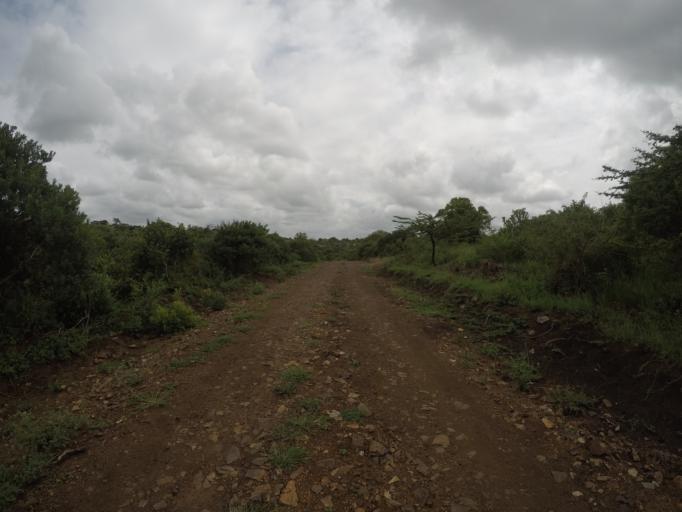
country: ZA
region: KwaZulu-Natal
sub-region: uThungulu District Municipality
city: Empangeni
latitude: -28.5852
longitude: 31.8687
